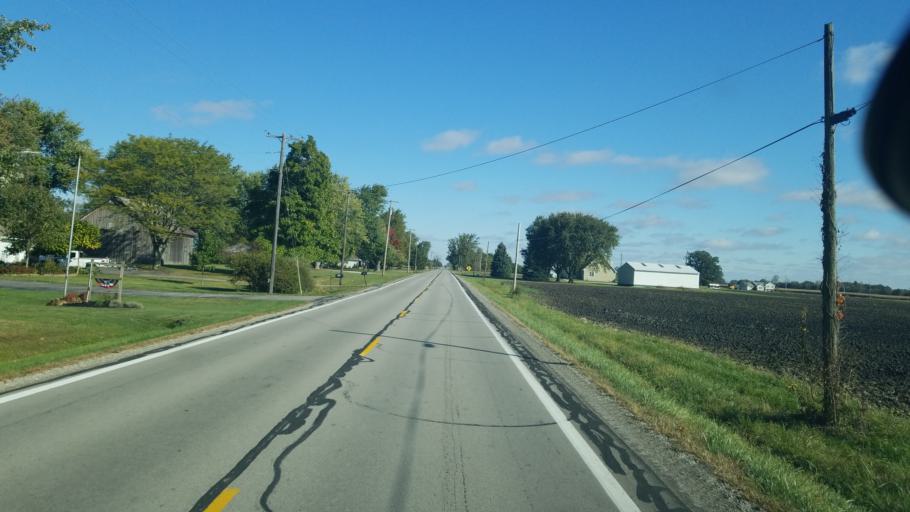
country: US
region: Ohio
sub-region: Marion County
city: Marion
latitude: 40.6342
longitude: -83.0244
